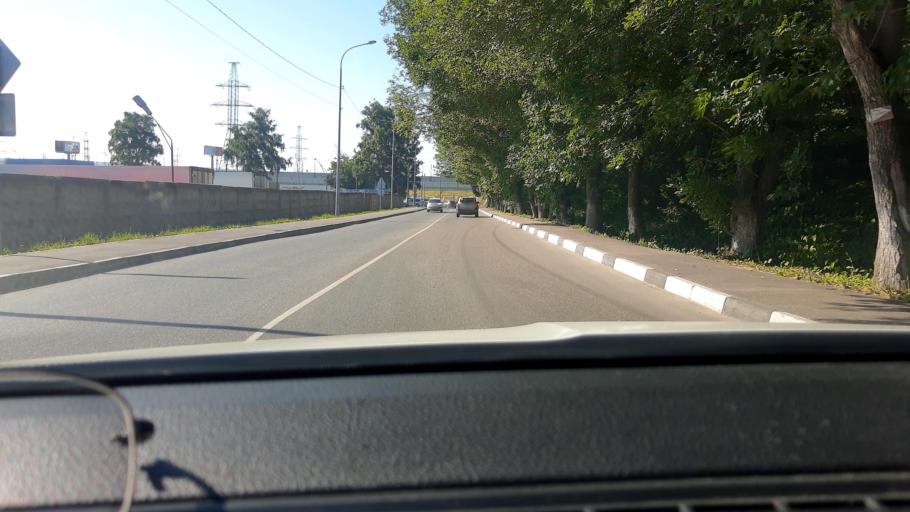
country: RU
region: Moskovskaya
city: Krasnogorsk
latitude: 55.8054
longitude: 37.3193
